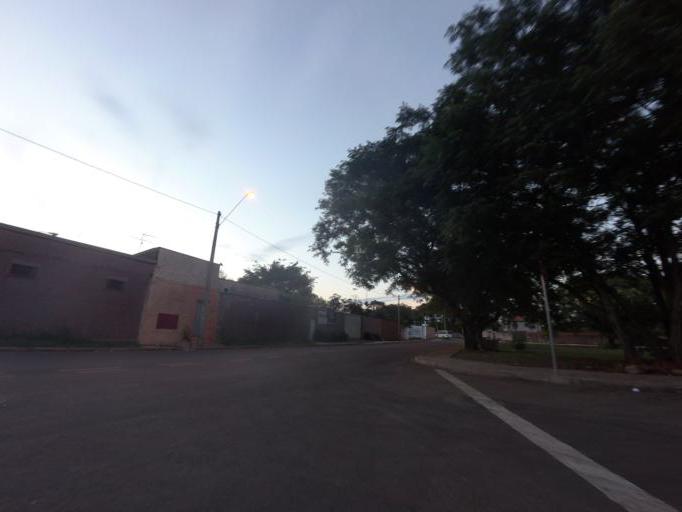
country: BR
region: Sao Paulo
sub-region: Piracicaba
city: Piracicaba
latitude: -22.7627
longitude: -47.5945
